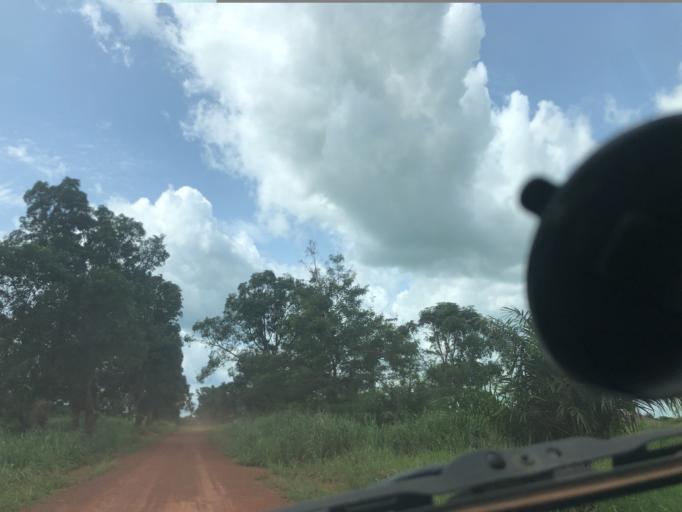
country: CF
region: Bangui
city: Bangui
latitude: 4.1240
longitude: 18.7847
